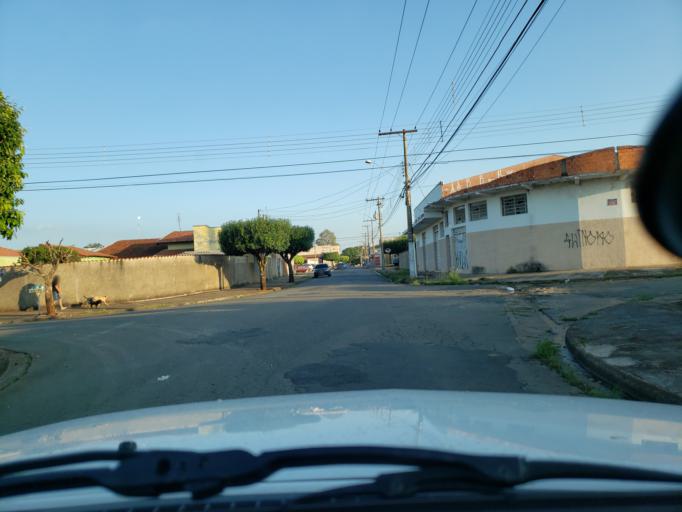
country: BR
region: Sao Paulo
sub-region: Moji-Guacu
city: Mogi-Gaucu
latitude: -22.3434
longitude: -46.9386
